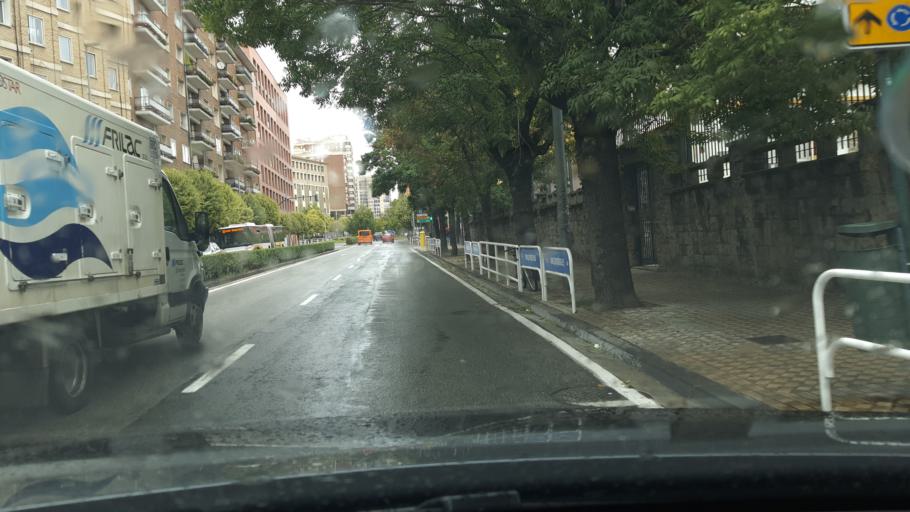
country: ES
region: Navarre
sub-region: Provincia de Navarra
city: Segundo Ensanche
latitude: 42.8049
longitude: -1.6443
